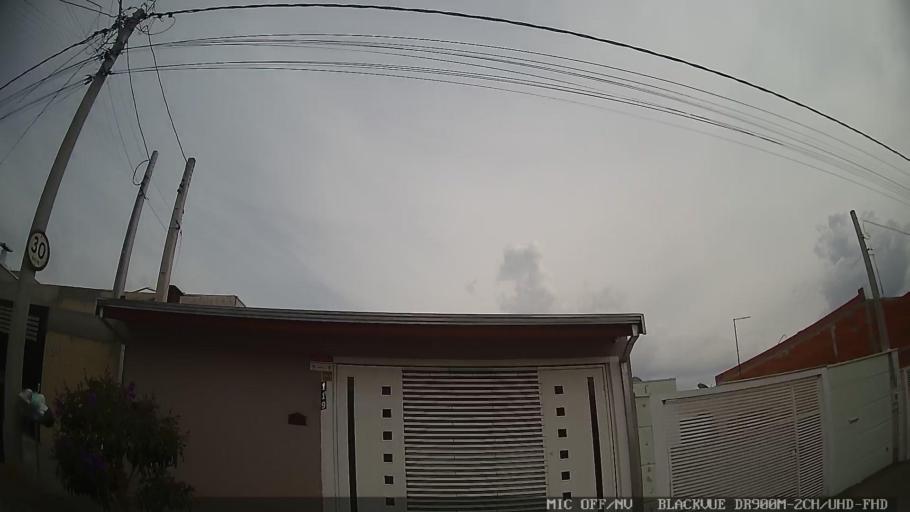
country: BR
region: Sao Paulo
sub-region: Indaiatuba
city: Indaiatuba
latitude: -23.0983
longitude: -47.2529
